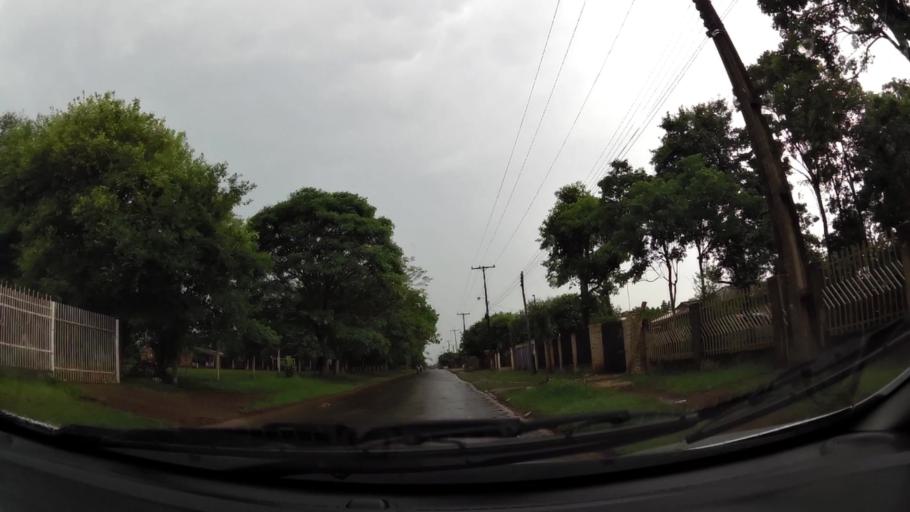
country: PY
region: Alto Parana
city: Presidente Franco
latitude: -25.5536
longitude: -54.6601
